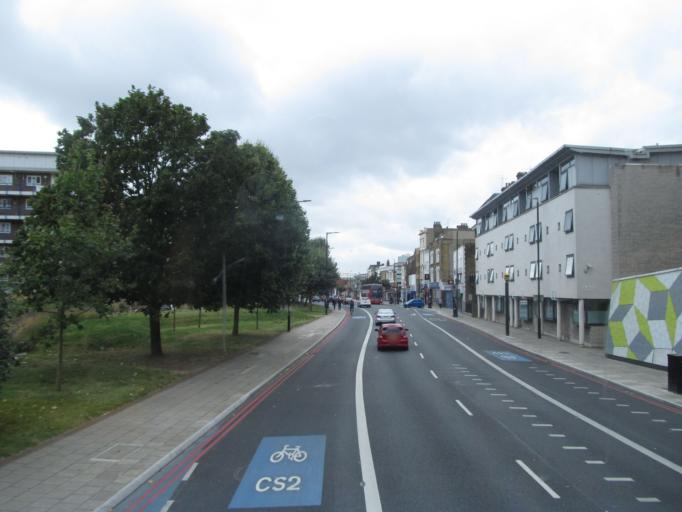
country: GB
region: England
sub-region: Greater London
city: Bethnal Green
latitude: 51.5223
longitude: -0.0432
